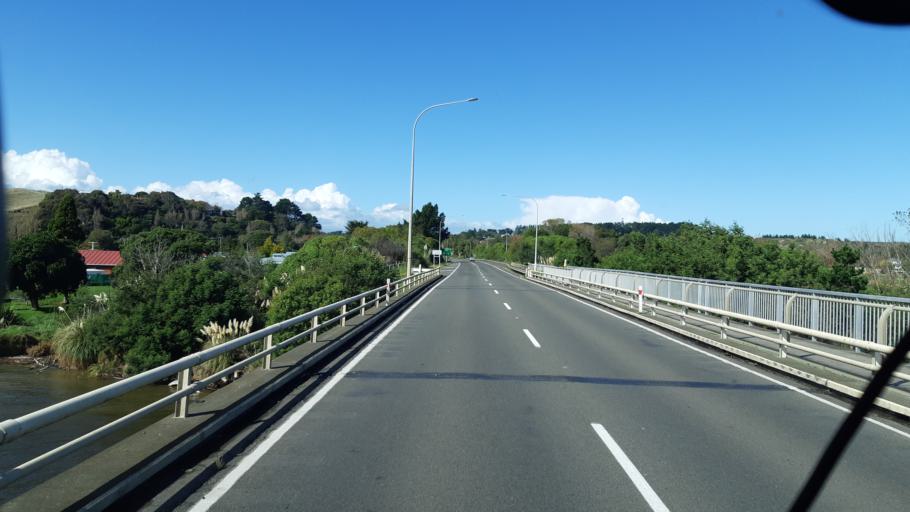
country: NZ
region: Manawatu-Wanganui
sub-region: Wanganui District
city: Wanganui
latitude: -39.9457
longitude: 175.0470
